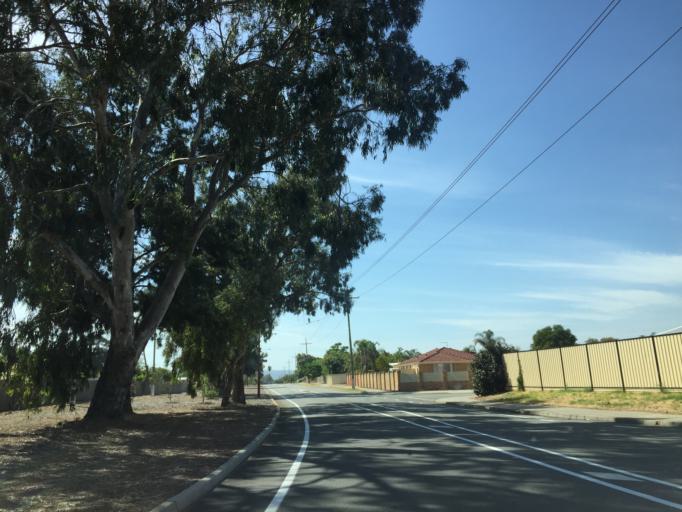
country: AU
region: Western Australia
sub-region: Gosnells
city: Thornlie
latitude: -32.0754
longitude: 115.9616
